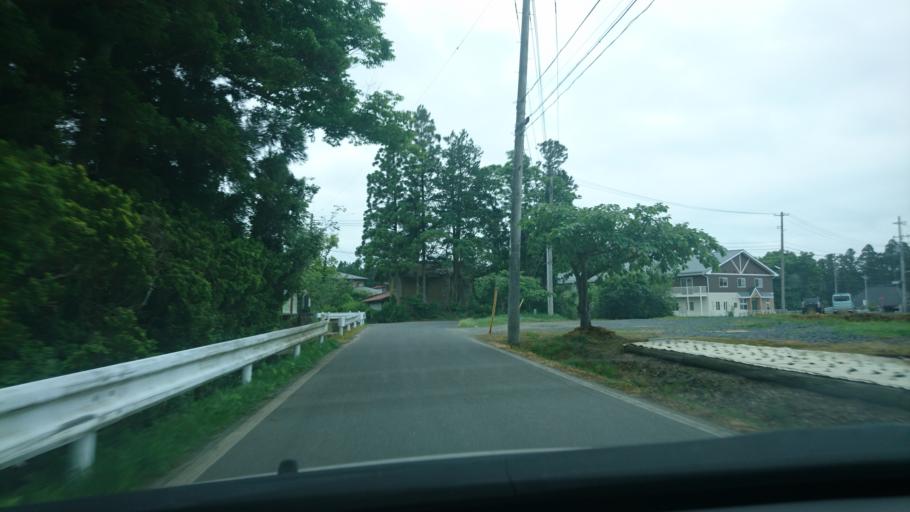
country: JP
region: Iwate
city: Ichinoseki
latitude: 38.9171
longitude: 141.0924
